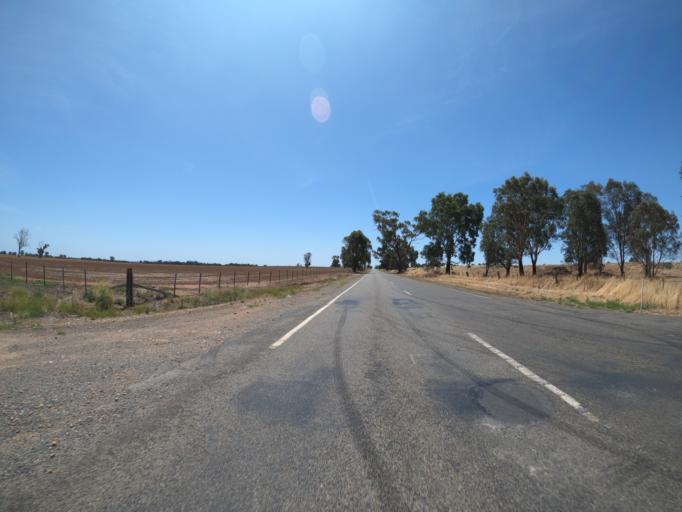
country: AU
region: Victoria
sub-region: Moira
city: Yarrawonga
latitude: -36.0552
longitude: 145.9954
